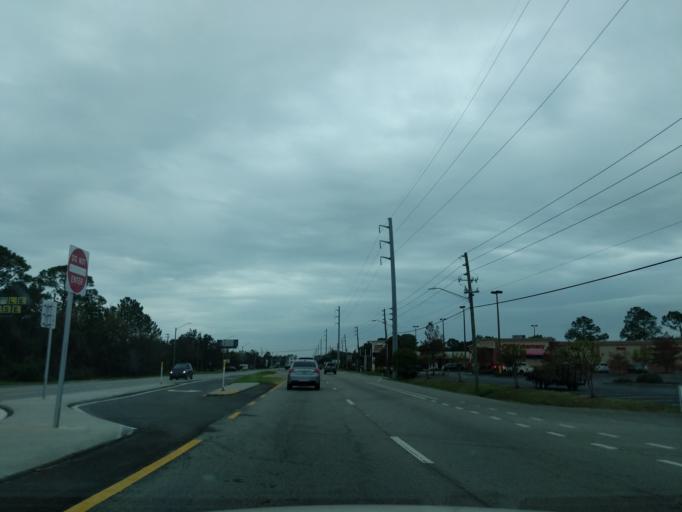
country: US
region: Florida
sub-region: Santa Rosa County
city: Oriole Beach
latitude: 30.3867
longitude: -87.0860
